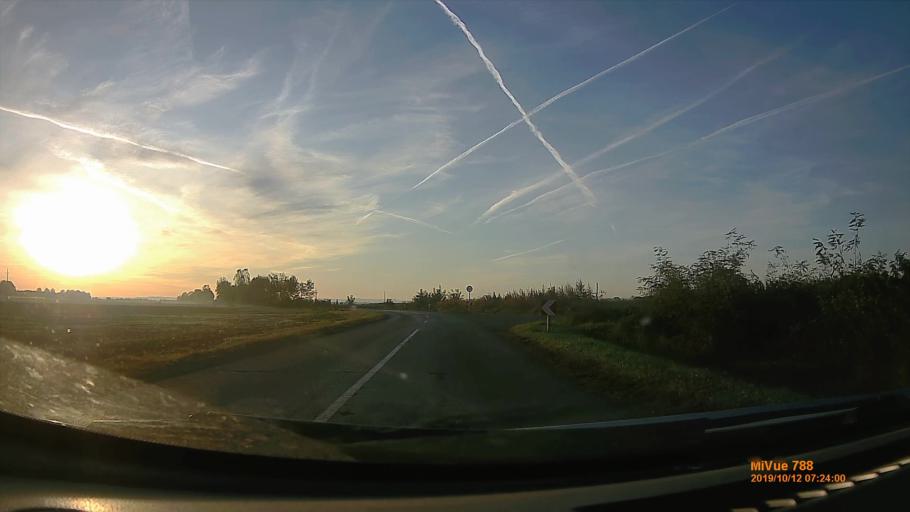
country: HU
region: Hajdu-Bihar
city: Hosszupalyi
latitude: 47.3586
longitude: 21.7496
